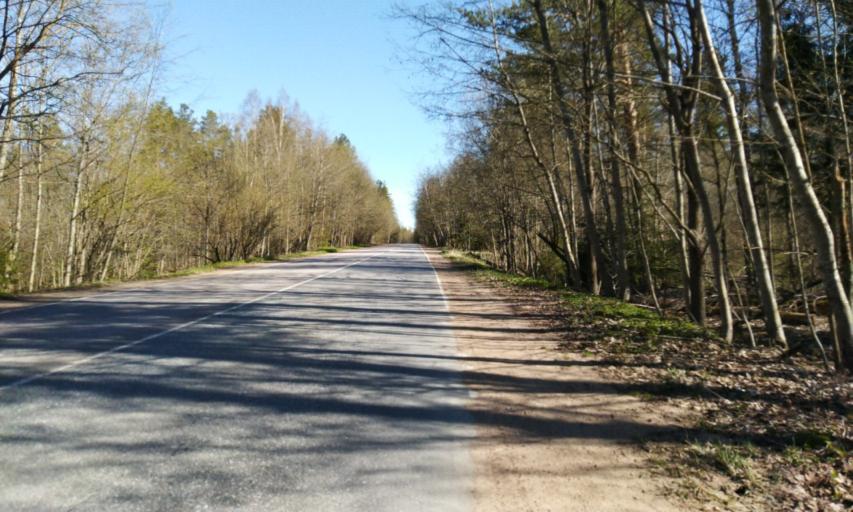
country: RU
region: Leningrad
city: Garbolovo
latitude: 60.3877
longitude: 30.4753
